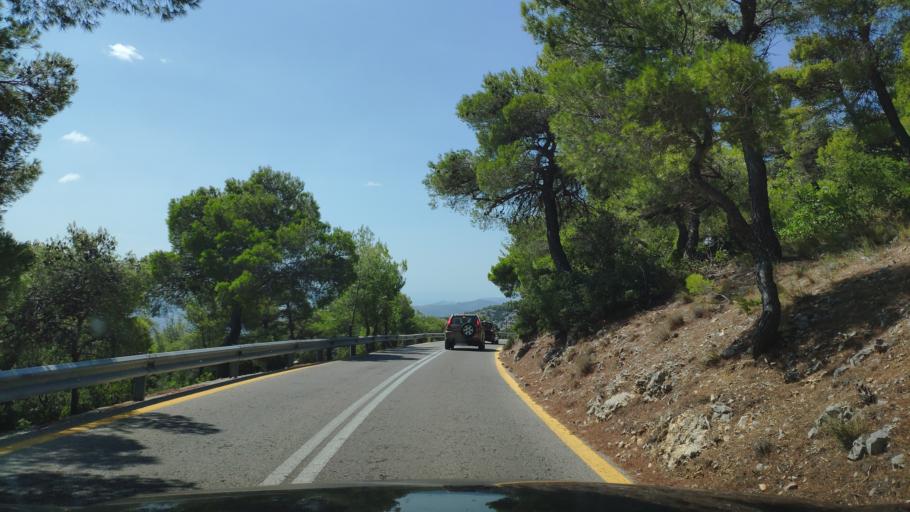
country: GR
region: Attica
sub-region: Nomarchia Anatolikis Attikis
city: Thrakomakedones
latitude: 38.1389
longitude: 23.7288
